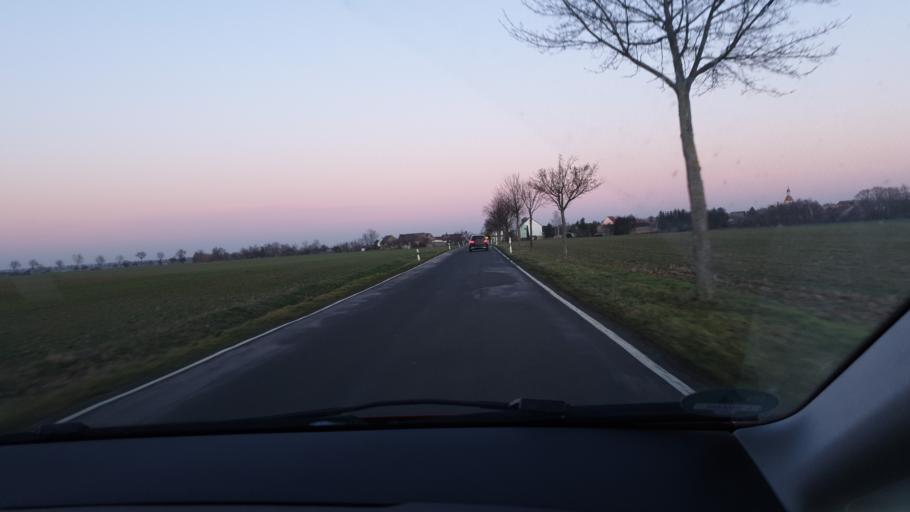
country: DE
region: Saxony
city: Mockrehna
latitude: 51.4691
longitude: 12.7986
